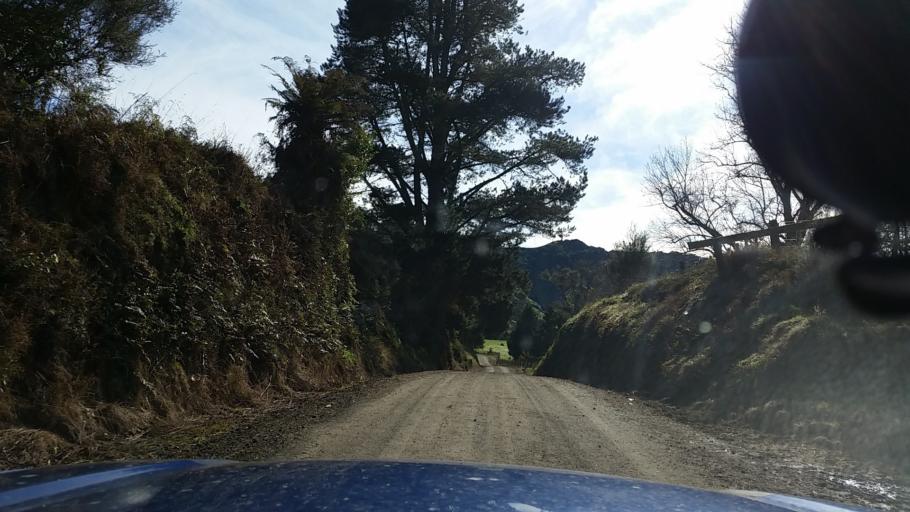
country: NZ
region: Taranaki
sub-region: New Plymouth District
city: Waitara
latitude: -39.0554
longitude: 174.7730
